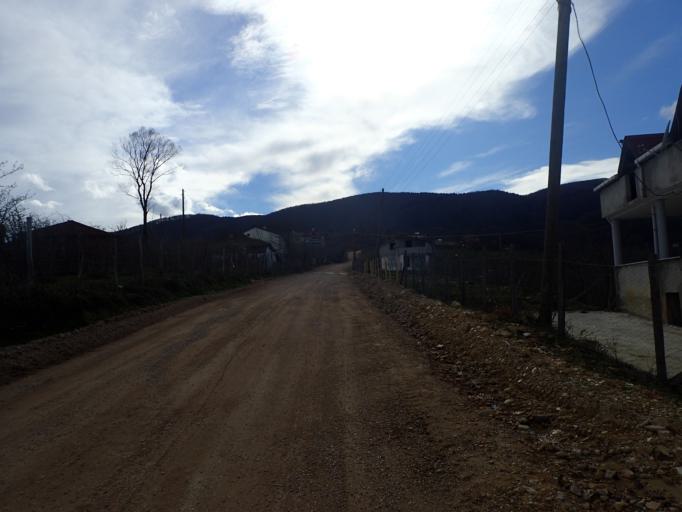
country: TR
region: Ordu
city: Kumru
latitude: 40.9306
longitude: 37.2521
